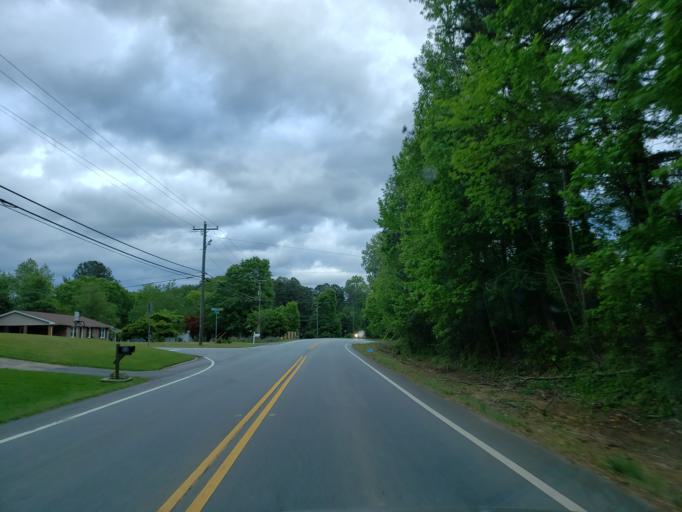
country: US
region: Georgia
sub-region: Paulding County
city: Dallas
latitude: 33.8730
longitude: -84.8549
